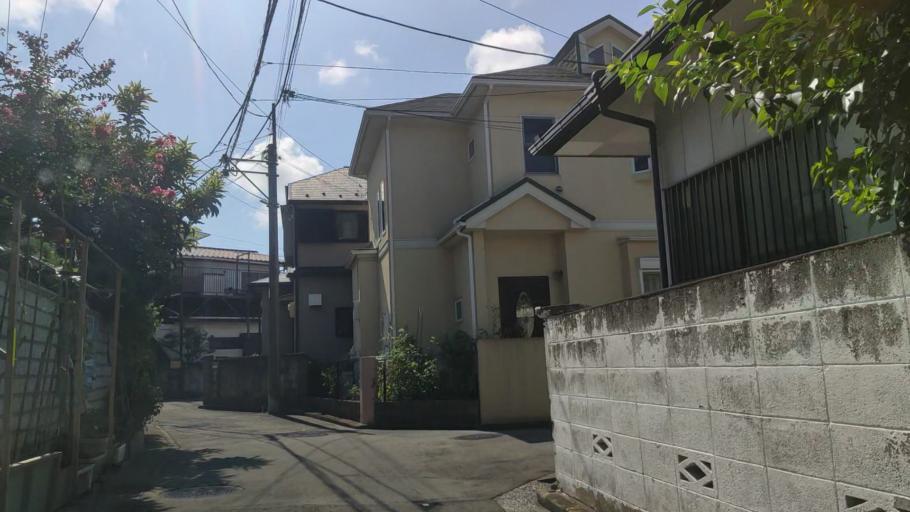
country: JP
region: Kanagawa
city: Yokohama
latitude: 35.4106
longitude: 139.5717
